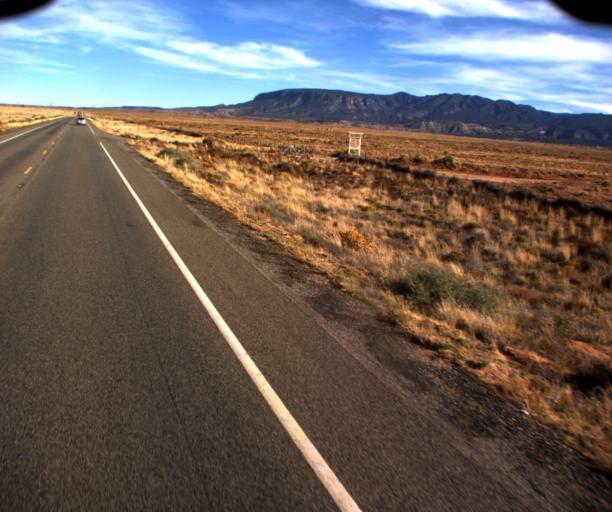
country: US
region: Arizona
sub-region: Apache County
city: Lukachukai
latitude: 36.9444
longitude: -109.2636
